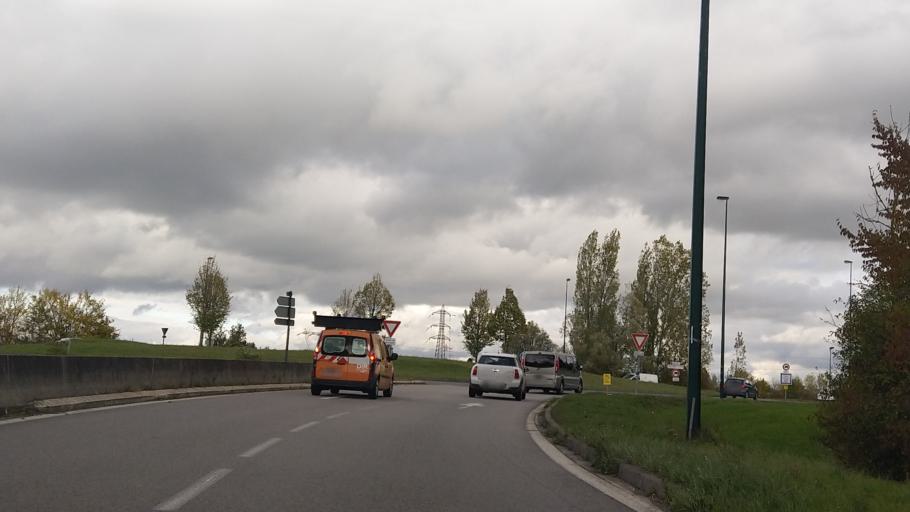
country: FR
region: Ile-de-France
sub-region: Departement du Val-d'Oise
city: Mours
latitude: 49.1276
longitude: 2.2569
